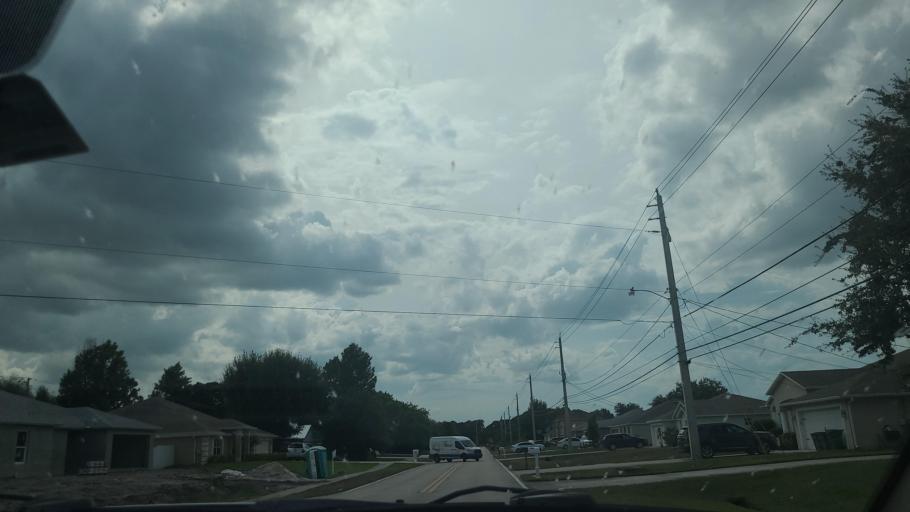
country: US
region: Florida
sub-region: Saint Lucie County
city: Port Saint Lucie
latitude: 27.2426
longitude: -80.3726
